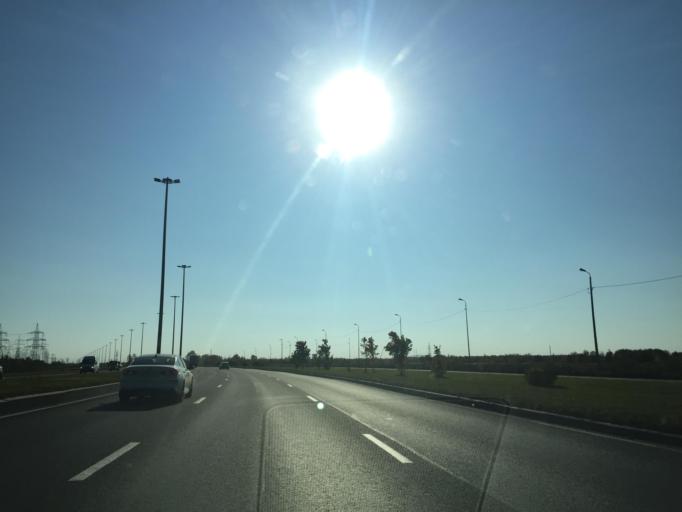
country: RU
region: St.-Petersburg
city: Petro-Slavyanka
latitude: 59.7671
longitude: 30.5016
